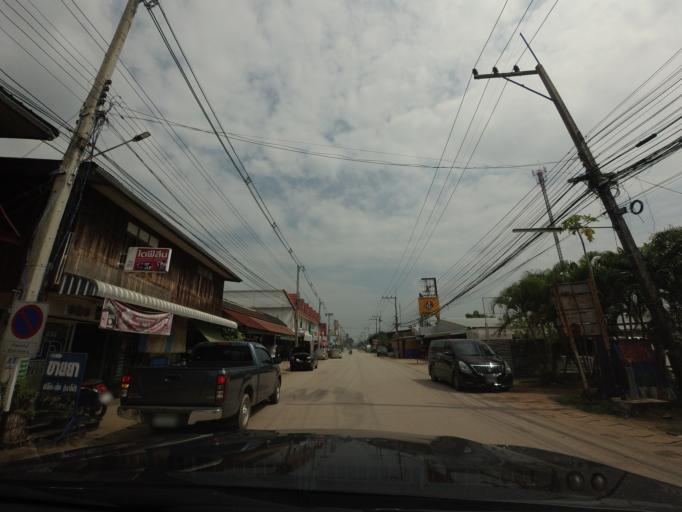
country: TH
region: Loei
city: Tha Li
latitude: 17.6257
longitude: 101.4228
